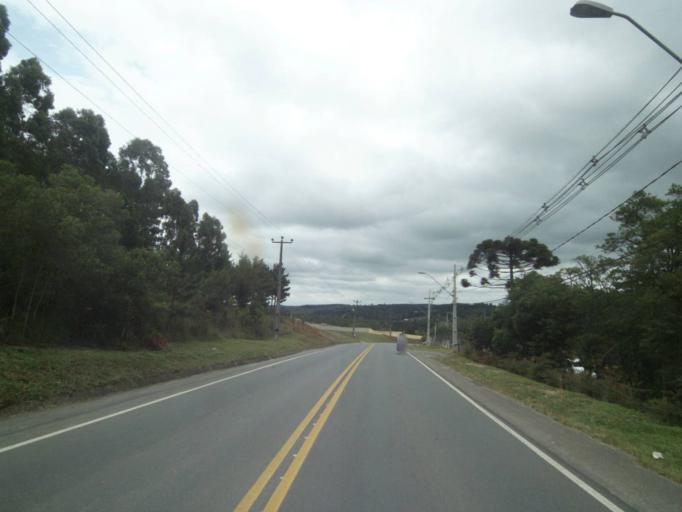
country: BR
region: Parana
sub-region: Campina Grande Do Sul
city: Campina Grande do Sul
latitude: -25.3130
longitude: -49.0692
